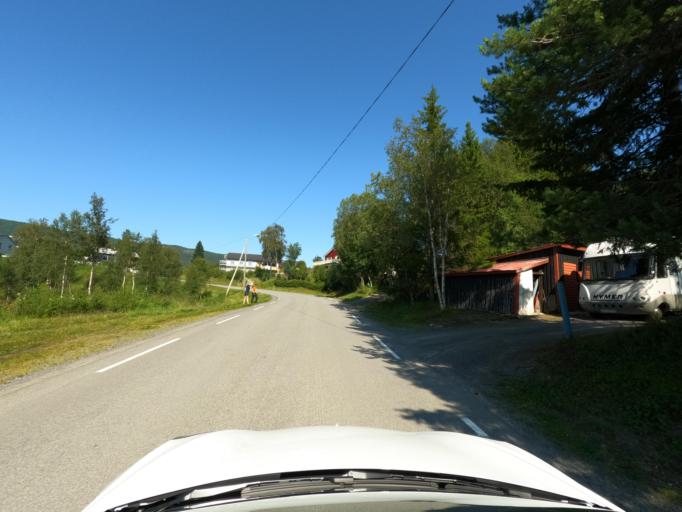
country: NO
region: Nordland
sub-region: Ballangen
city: Ballangen
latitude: 68.3422
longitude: 16.8217
